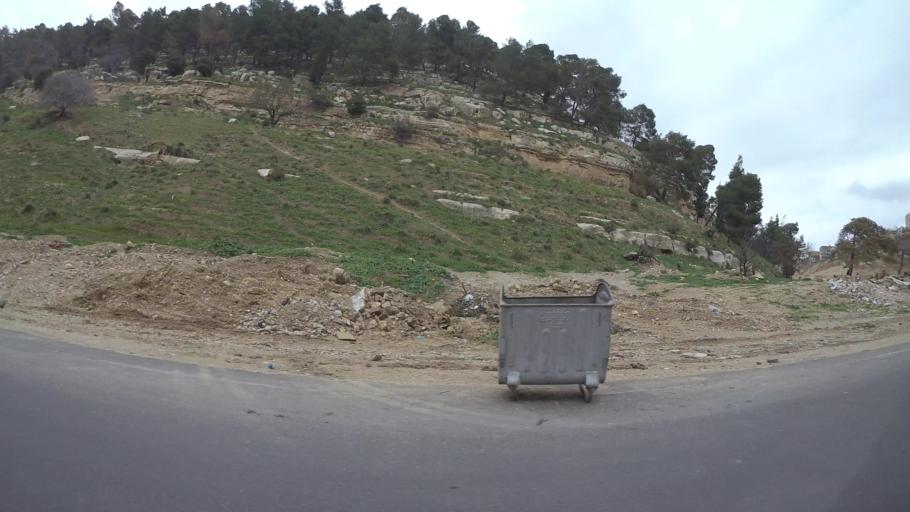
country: JO
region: Amman
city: Wadi as Sir
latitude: 31.9564
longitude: 35.8220
